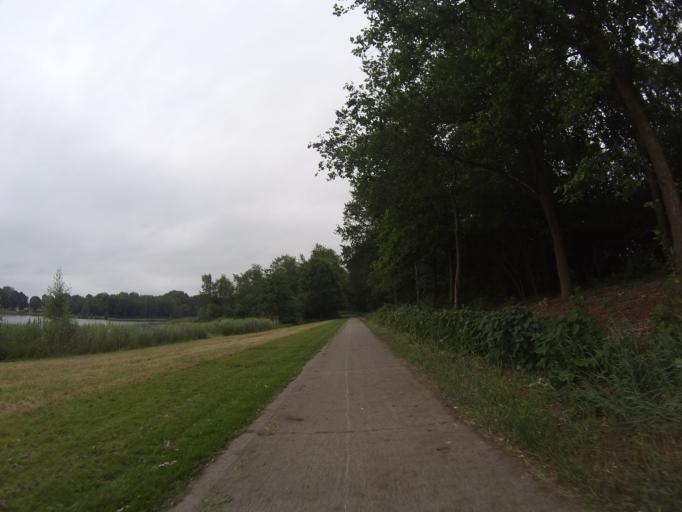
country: NL
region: Drenthe
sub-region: Gemeente Emmen
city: Emmer-Compascuum
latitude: 52.8039
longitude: 7.0362
